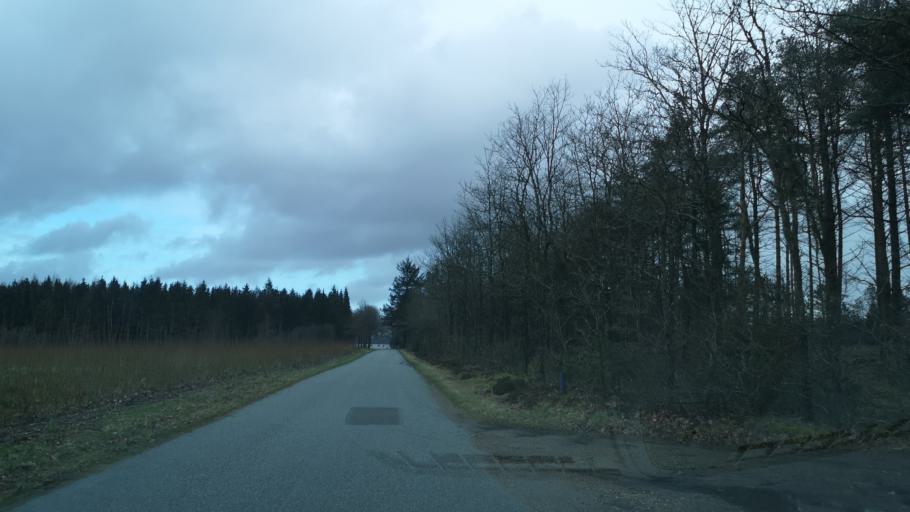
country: DK
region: Central Jutland
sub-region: Herning Kommune
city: Lind
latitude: 55.9992
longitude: 8.9690
